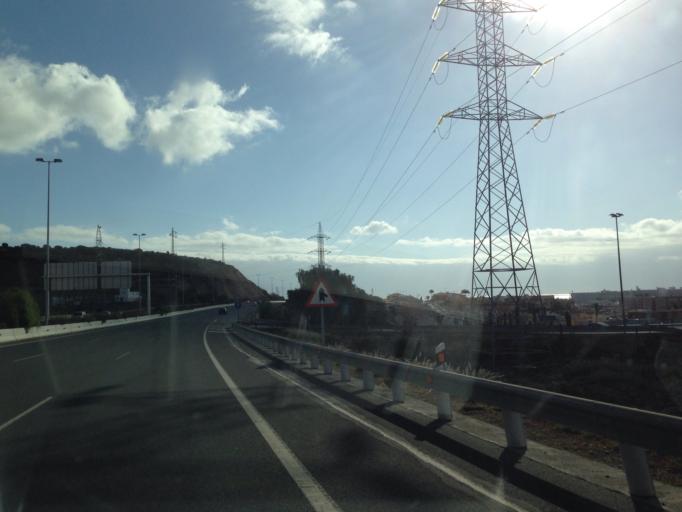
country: ES
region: Canary Islands
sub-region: Provincia de Las Palmas
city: Maspalomas
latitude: 27.7724
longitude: -15.5795
